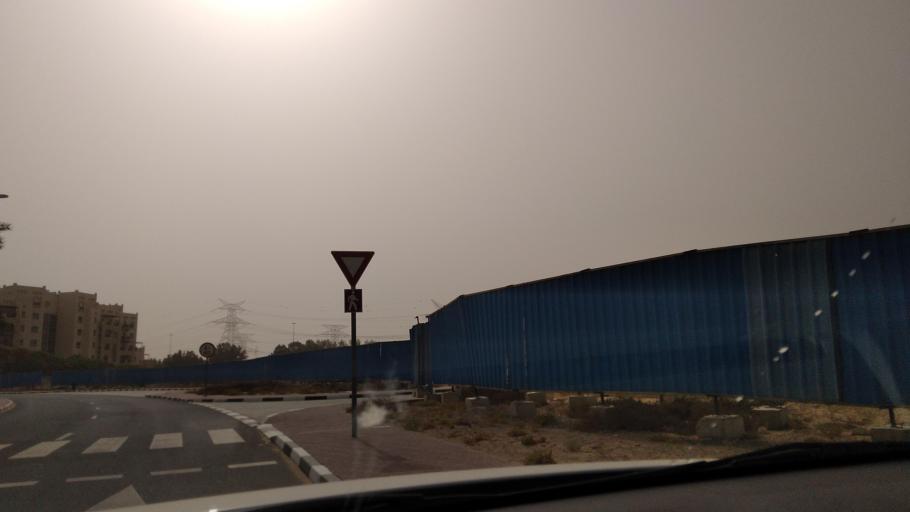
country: AE
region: Dubai
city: Dubai
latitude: 24.9993
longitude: 55.2526
